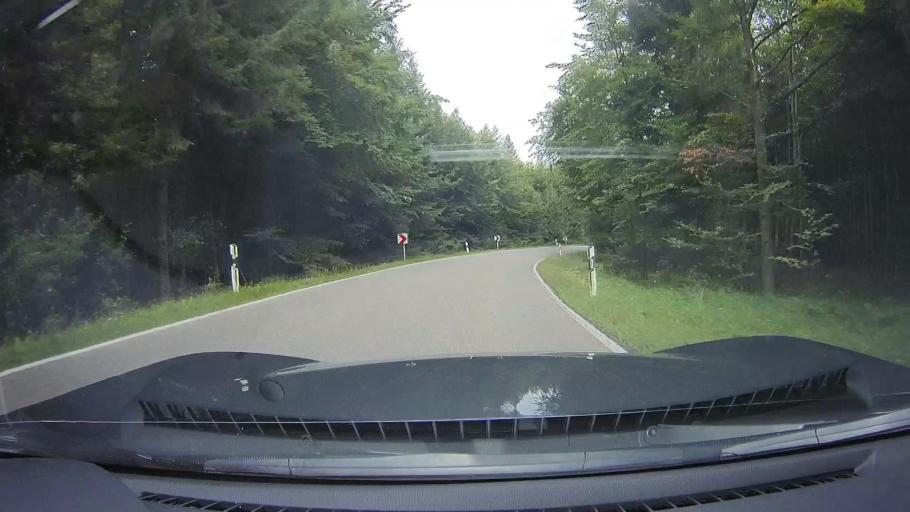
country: DE
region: Baden-Wuerttemberg
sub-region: Regierungsbezirk Stuttgart
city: Kaisersbach
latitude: 48.9404
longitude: 9.6074
